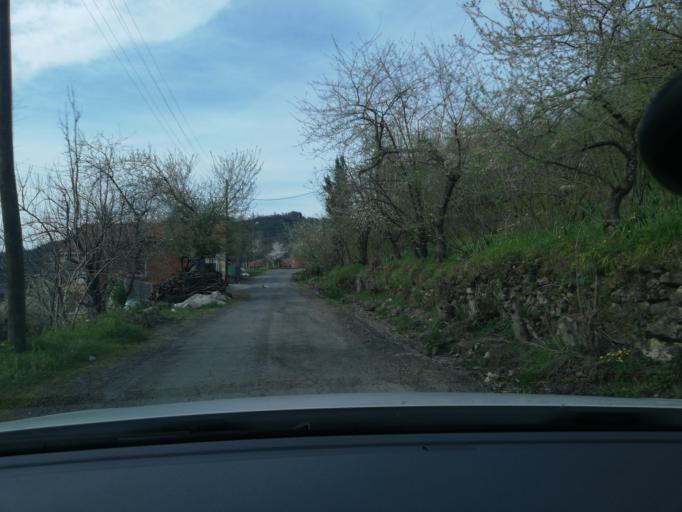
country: TR
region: Zonguldak
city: Kozlu
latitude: 41.3592
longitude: 31.6330
